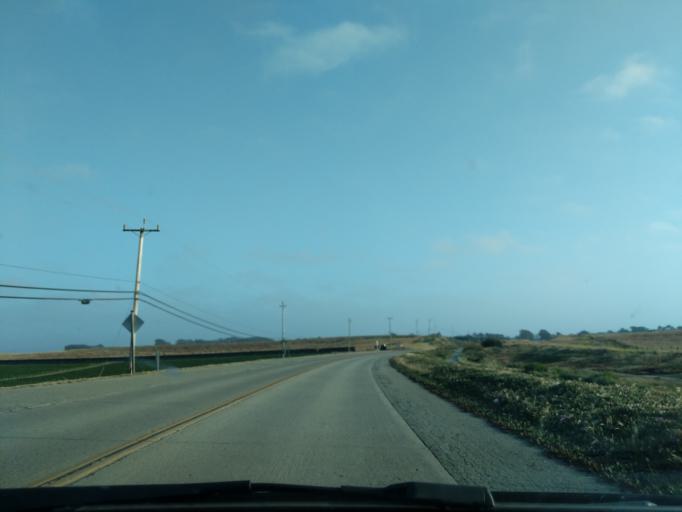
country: US
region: California
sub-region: Monterey County
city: Marina
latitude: 36.7040
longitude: -121.7889
